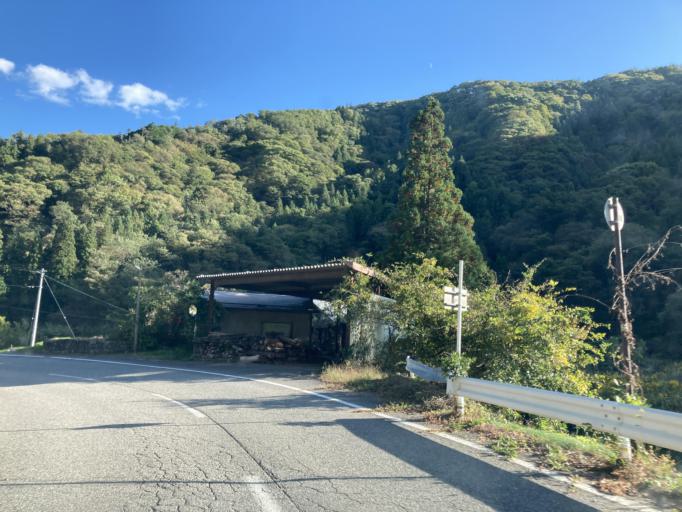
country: JP
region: Nagano
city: Omachi
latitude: 36.4703
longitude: 137.9408
